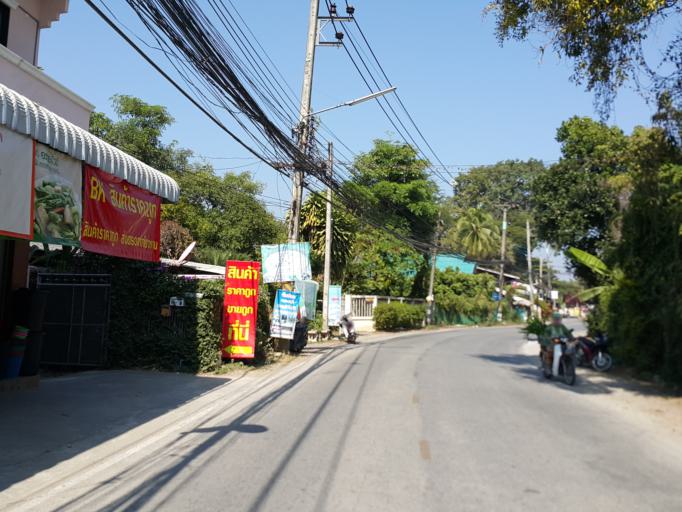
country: TH
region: Chiang Mai
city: Chiang Mai
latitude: 18.8234
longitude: 98.9992
